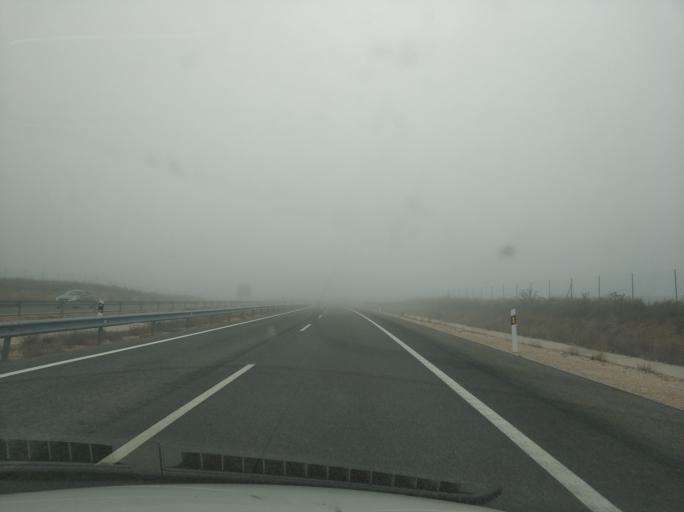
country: ES
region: Castille and Leon
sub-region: Provincia de Soria
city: Adradas
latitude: 41.3356
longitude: -2.4819
